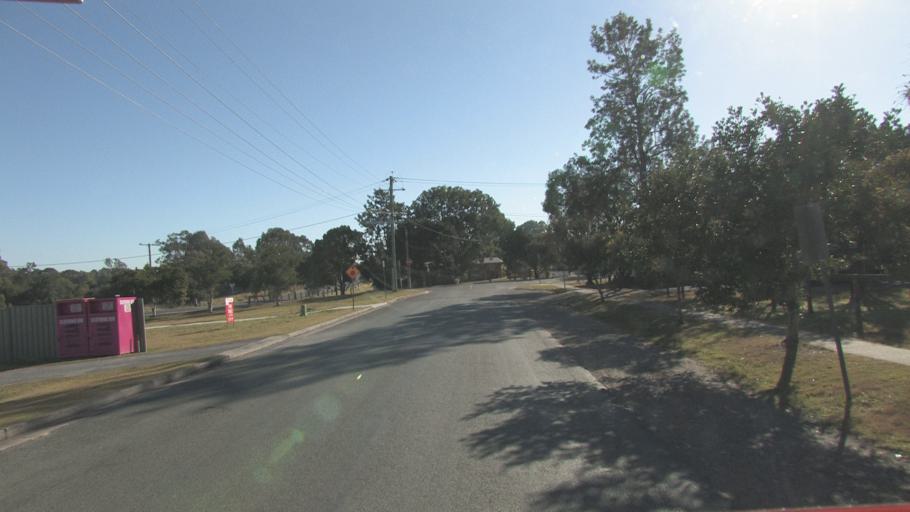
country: AU
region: Queensland
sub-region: Logan
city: Chambers Flat
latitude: -27.7659
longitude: 153.1051
